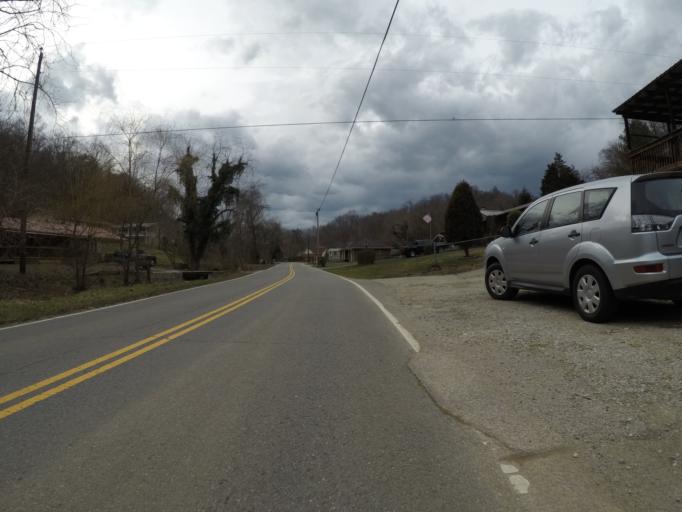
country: US
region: Ohio
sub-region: Lawrence County
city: Burlington
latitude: 38.4253
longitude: -82.5092
